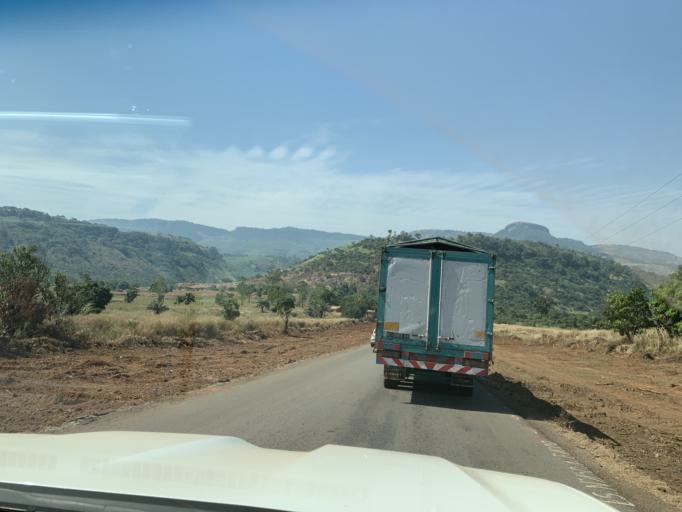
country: GN
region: Mamou
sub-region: Mamou Prefecture
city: Mamou
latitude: 10.1953
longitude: -12.4614
